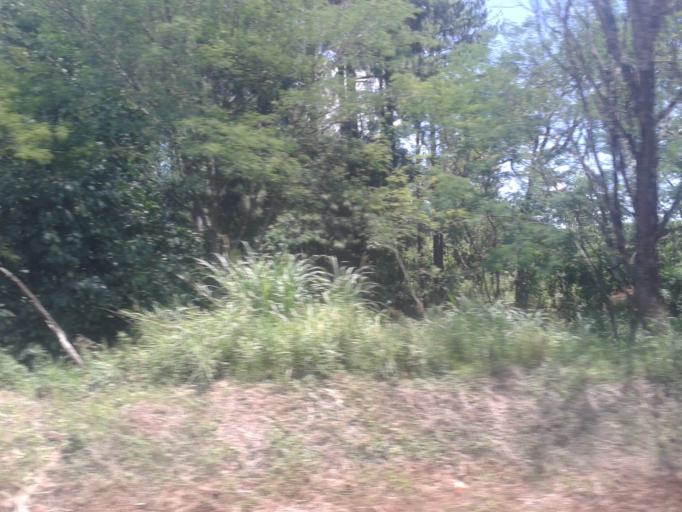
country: AR
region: Misiones
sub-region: Departamento de Leandro N. Alem
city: Leandro N. Alem
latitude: -27.6190
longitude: -55.3331
